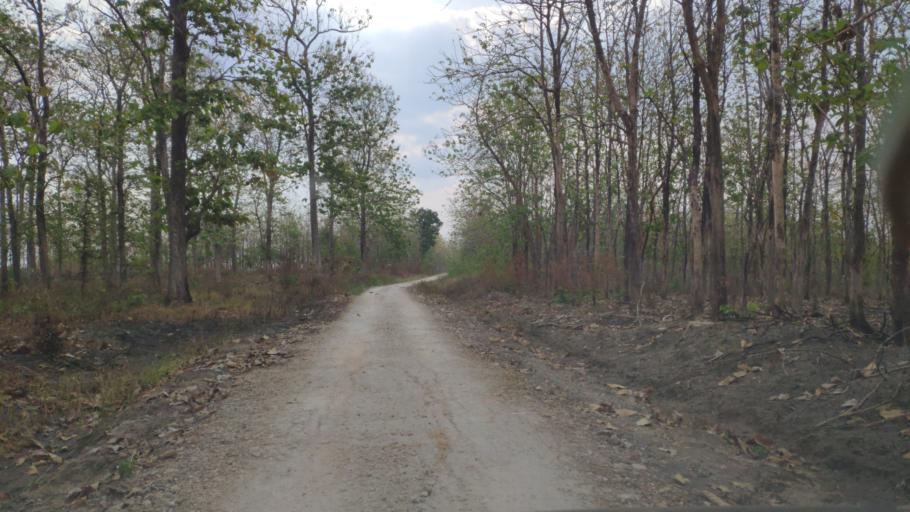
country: ID
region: Central Java
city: Randublatung
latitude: -7.3036
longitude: 111.3494
